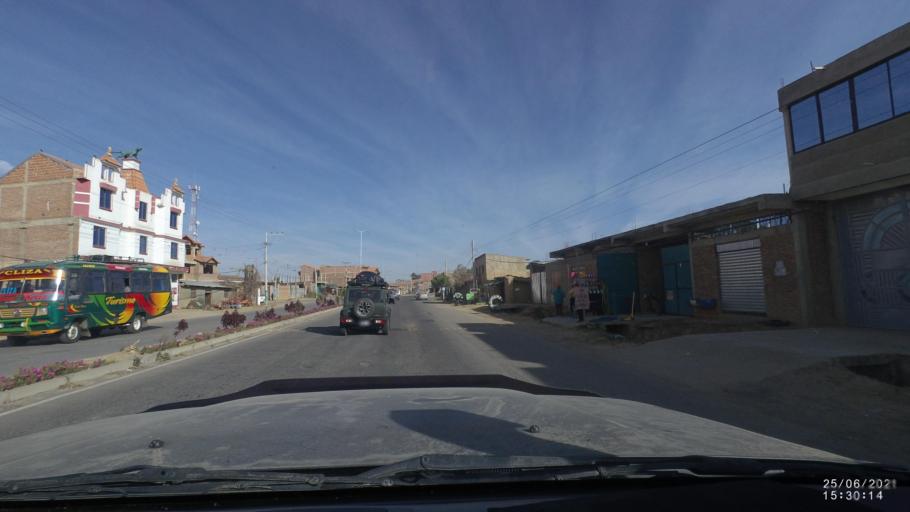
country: BO
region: Cochabamba
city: Cliza
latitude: -17.5819
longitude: -65.9336
